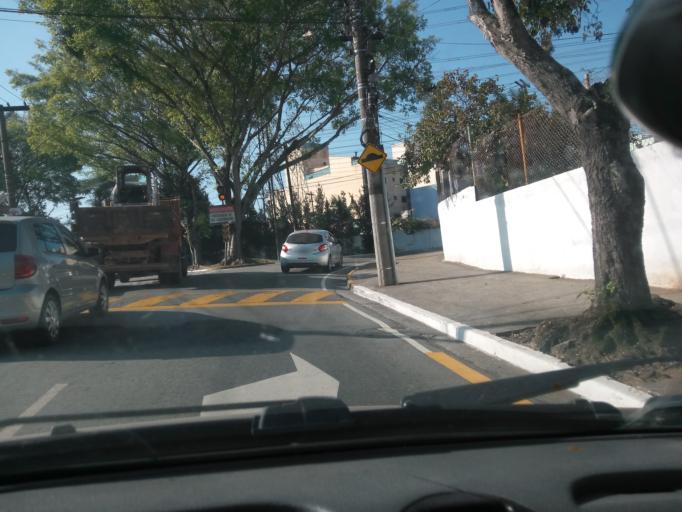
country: BR
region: Sao Paulo
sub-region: Sao Caetano Do Sul
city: Sao Caetano do Sul
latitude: -23.6397
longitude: -46.5737
